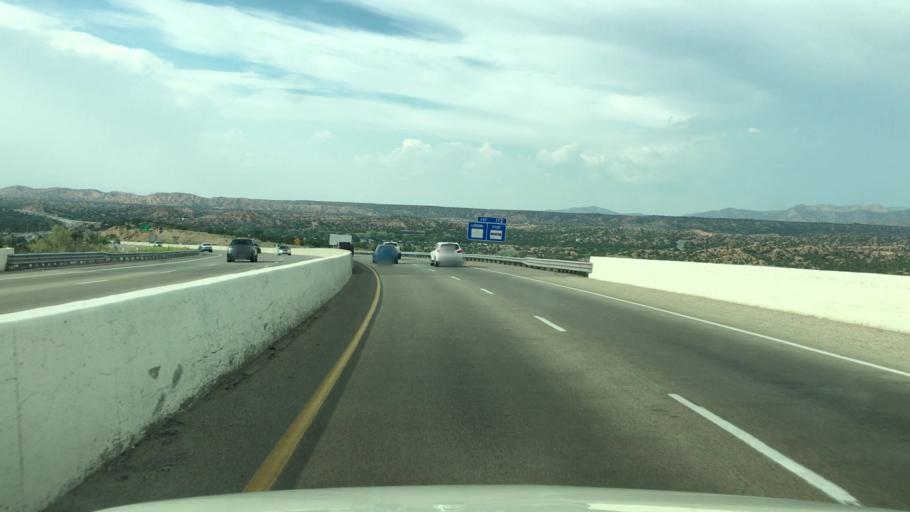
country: US
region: New Mexico
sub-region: Santa Fe County
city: Santa Fe
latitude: 35.7692
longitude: -105.9437
